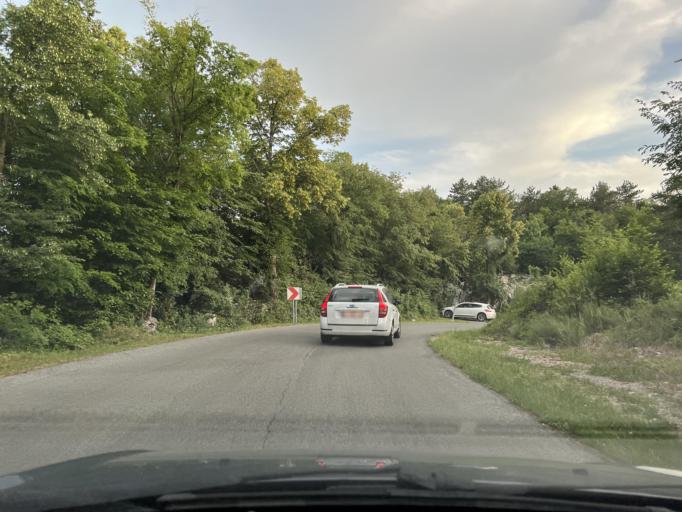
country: HR
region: Primorsko-Goranska
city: Marcelji
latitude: 45.3880
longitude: 14.4172
